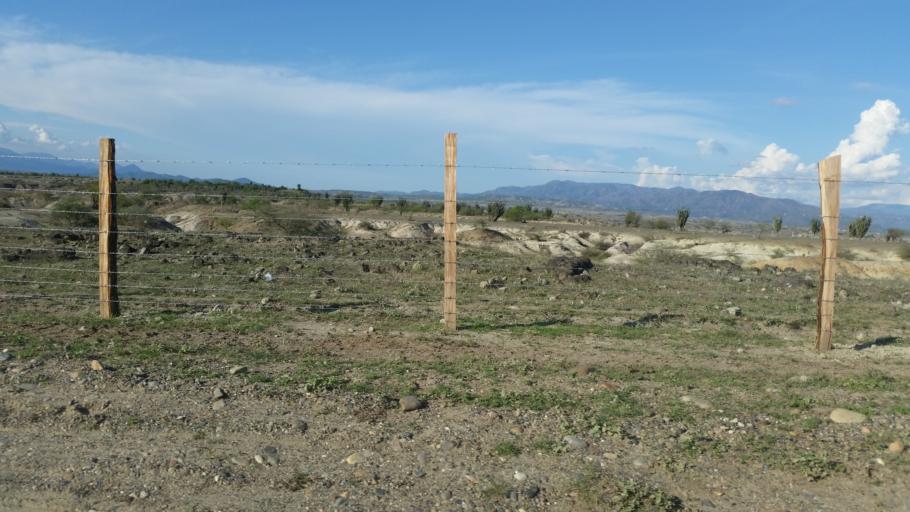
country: CO
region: Huila
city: Villavieja
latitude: 3.2326
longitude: -75.1578
